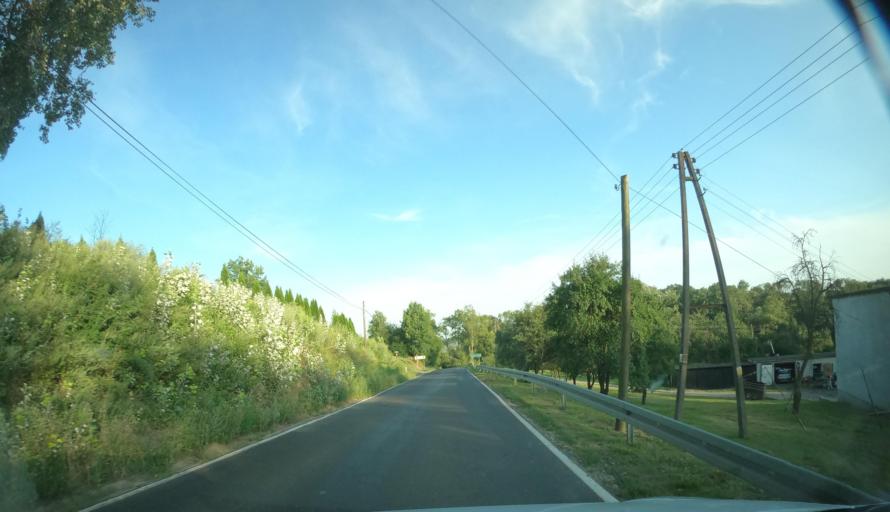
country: PL
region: Kujawsko-Pomorskie
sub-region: Bydgoszcz
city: Fordon
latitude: 53.2098
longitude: 18.1690
